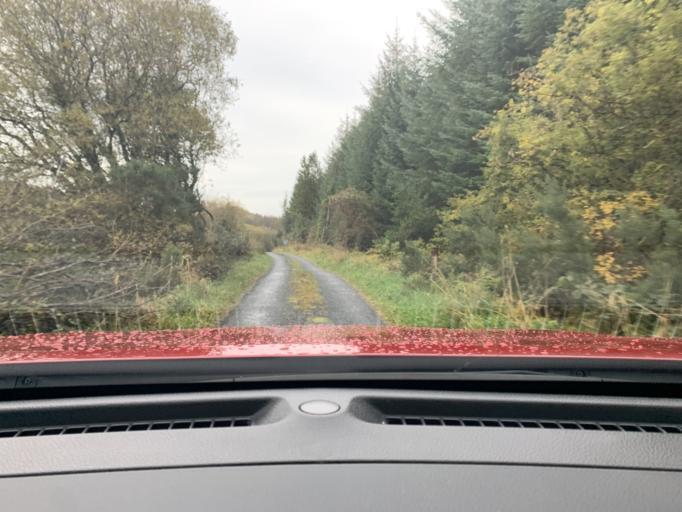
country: IE
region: Connaught
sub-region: Roscommon
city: Ballaghaderreen
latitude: 53.9243
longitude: -8.5651
